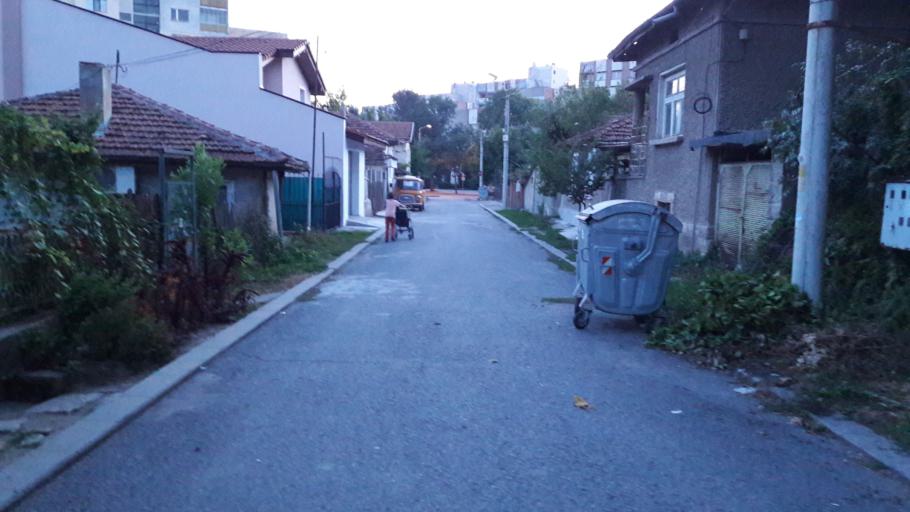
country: BG
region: Razgrad
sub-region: Obshtina Razgrad
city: Razgrad
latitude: 43.5308
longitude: 26.5258
